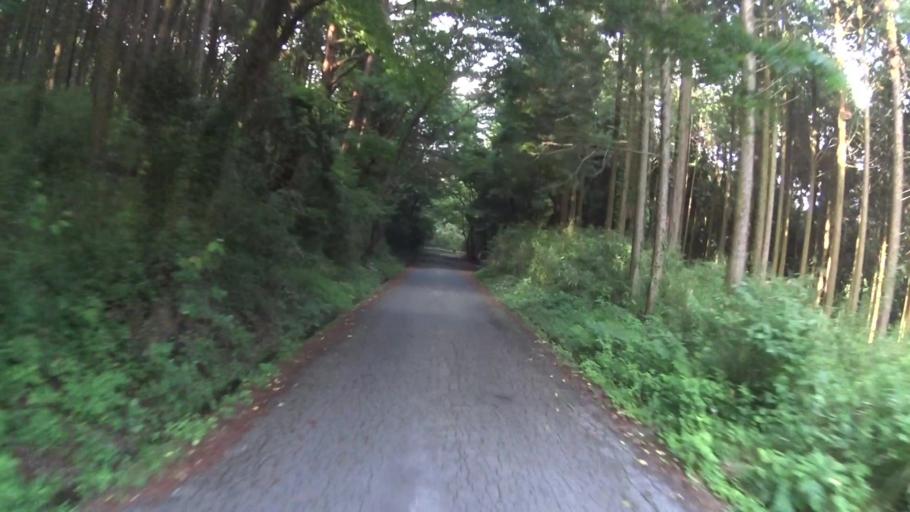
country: JP
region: Kumamoto
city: Aso
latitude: 32.9553
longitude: 131.0072
